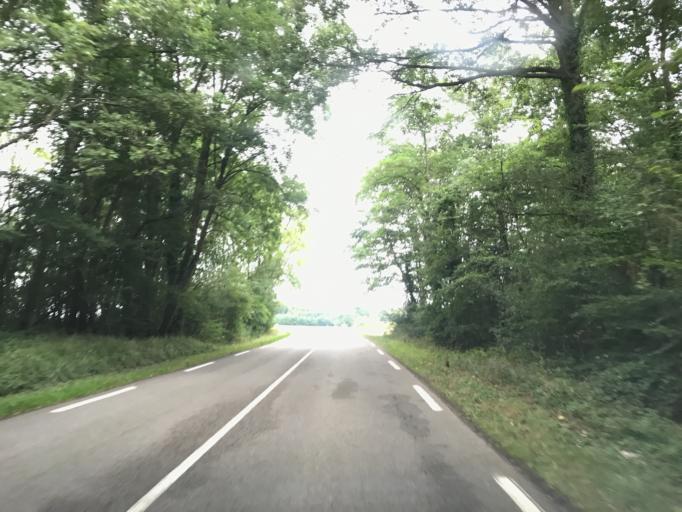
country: FR
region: Haute-Normandie
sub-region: Departement de l'Eure
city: Menilles
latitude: 49.0323
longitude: 1.2765
